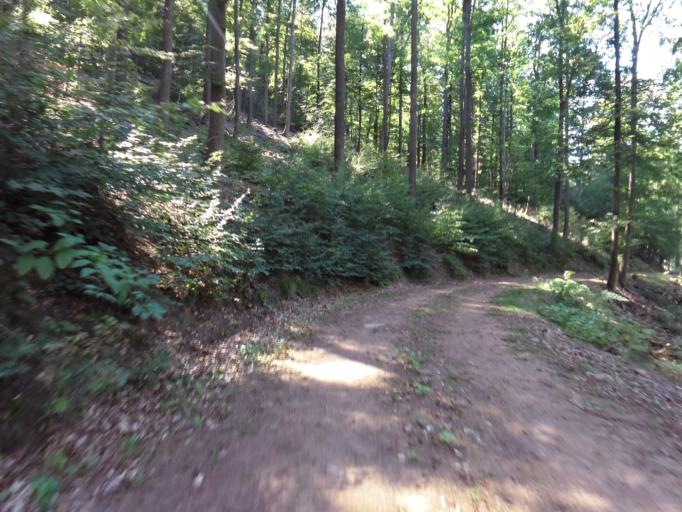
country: DE
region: Rheinland-Pfalz
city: Esthal
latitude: 49.3973
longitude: 7.9866
